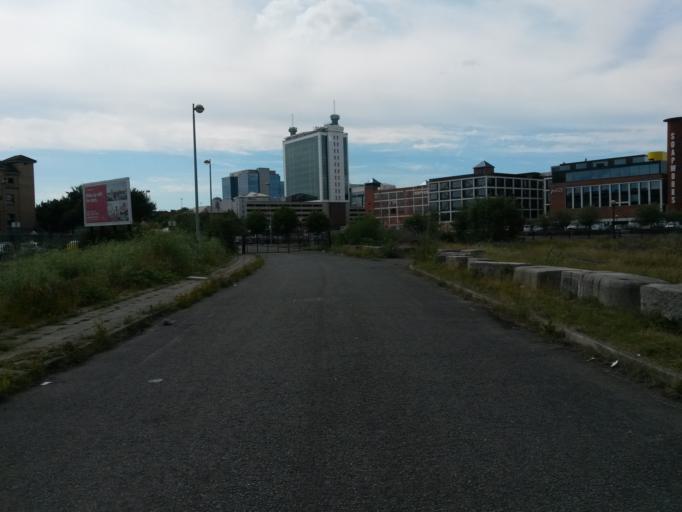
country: GB
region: England
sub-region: City and Borough of Salford
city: Salford
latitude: 53.4662
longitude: -2.2758
